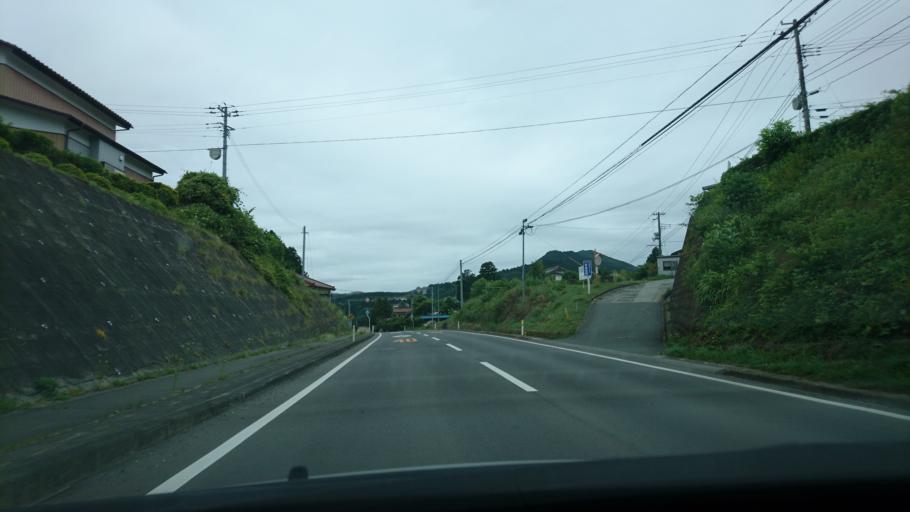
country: JP
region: Iwate
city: Ofunato
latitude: 38.7932
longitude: 141.5099
